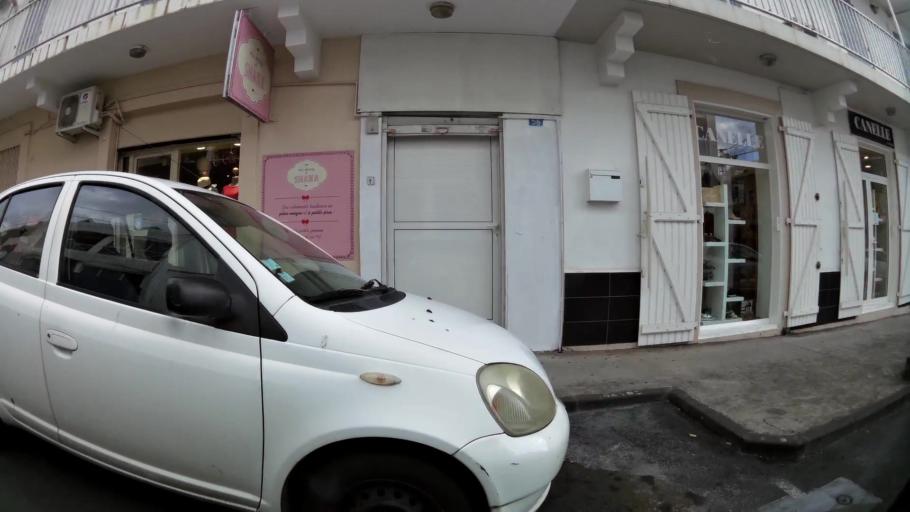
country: RE
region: Reunion
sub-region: Reunion
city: Saint-Denis
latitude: -20.8776
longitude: 55.4524
